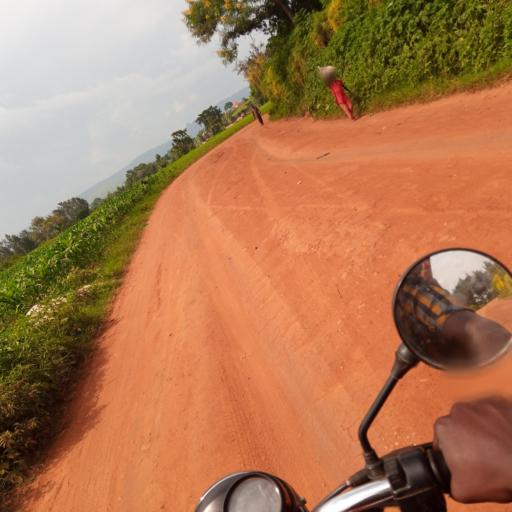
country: UG
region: Eastern Region
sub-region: Mbale District
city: Mbale
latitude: 1.0944
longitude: 34.1880
